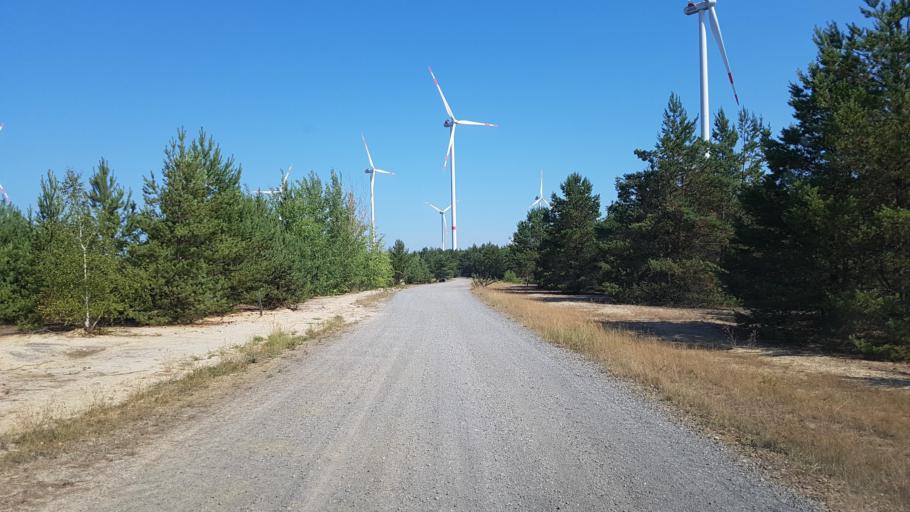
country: DE
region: Brandenburg
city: Schipkau
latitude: 51.5366
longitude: 13.8625
